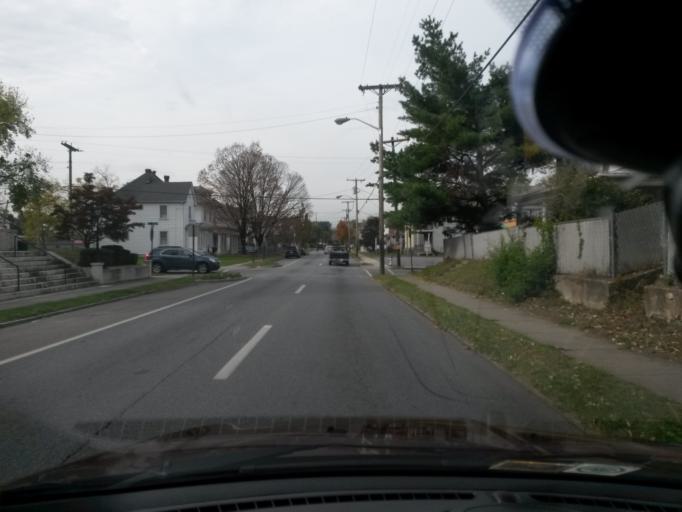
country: US
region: Virginia
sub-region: City of Roanoke
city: Cedar Bluff
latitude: 37.2701
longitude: -79.9253
